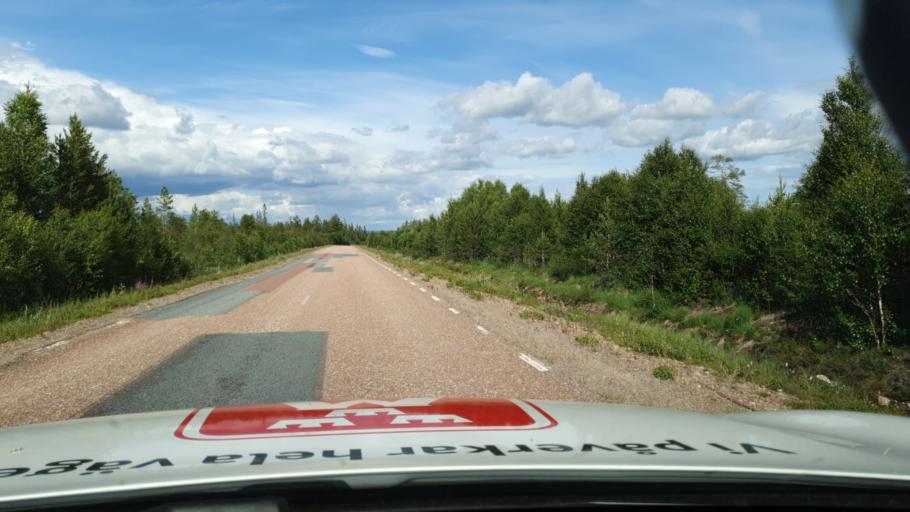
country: SE
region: Dalarna
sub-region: Alvdalens Kommun
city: AElvdalen
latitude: 61.7827
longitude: 13.4874
